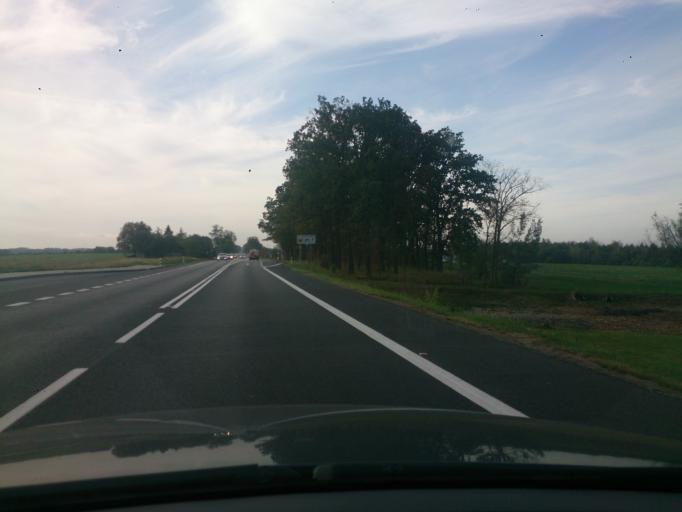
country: PL
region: Kujawsko-Pomorskie
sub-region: Powiat swiecki
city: Pruszcz
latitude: 53.3449
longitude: 18.2983
